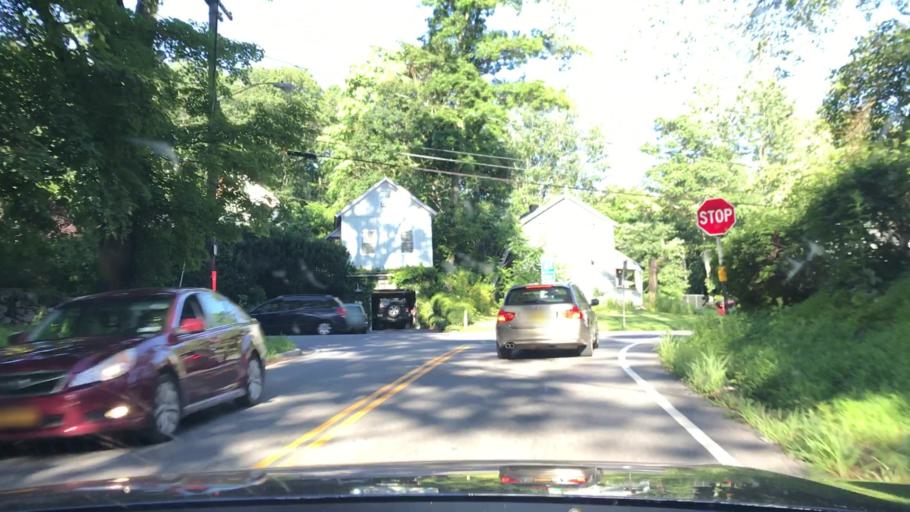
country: US
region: New York
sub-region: Westchester County
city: Heritage Hills
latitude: 41.3503
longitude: -73.6638
